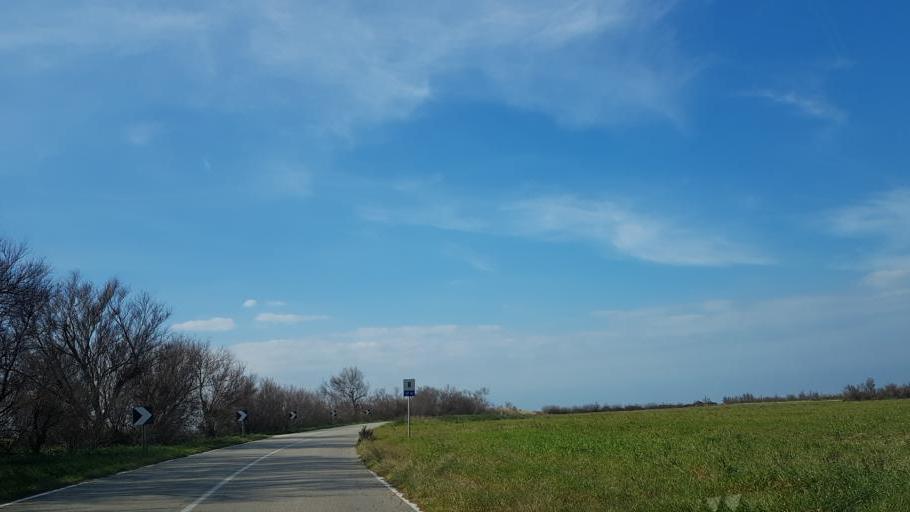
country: IT
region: Apulia
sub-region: Provincia di Brindisi
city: Brindisi
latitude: 40.6851
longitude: 17.8621
